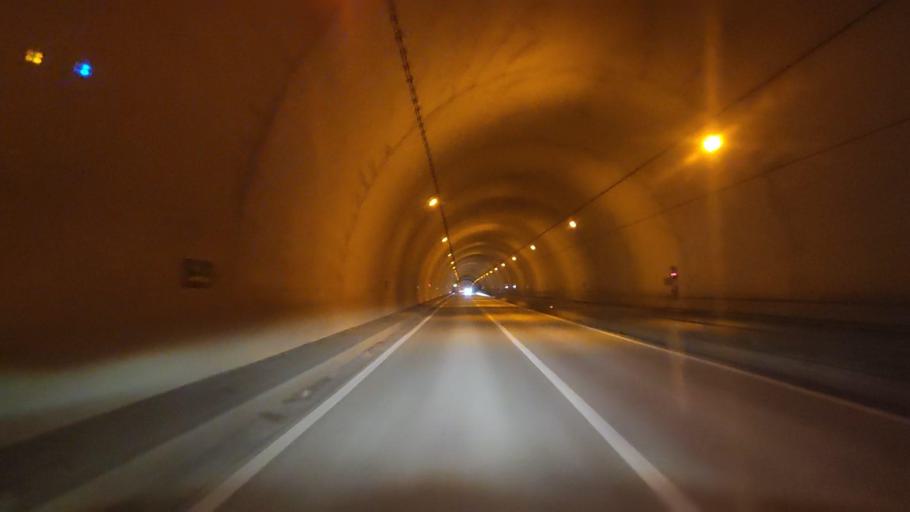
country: JP
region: Kumamoto
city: Hitoyoshi
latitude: 32.3927
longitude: 130.8280
